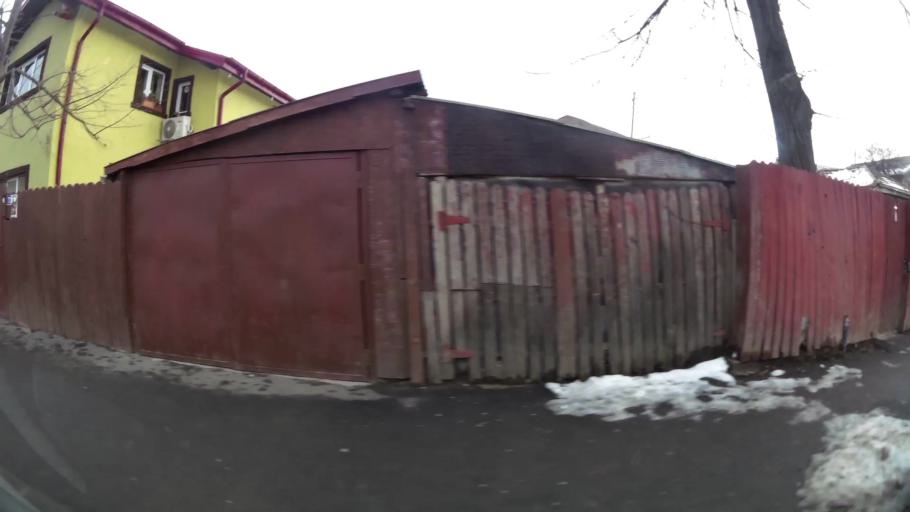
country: RO
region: Ilfov
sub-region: Comuna Pantelimon
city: Pantelimon
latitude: 44.4547
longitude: 26.1999
